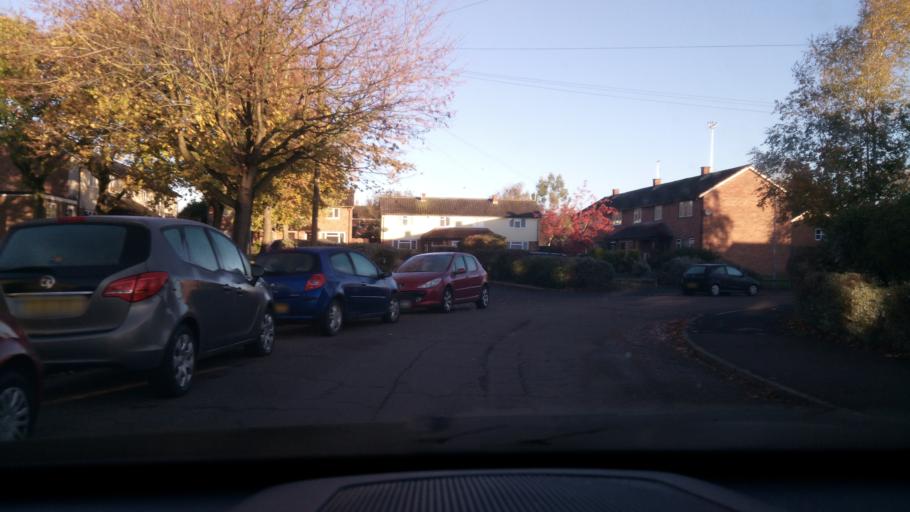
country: GB
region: England
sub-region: Peterborough
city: Wittering
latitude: 52.6074
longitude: -0.4357
